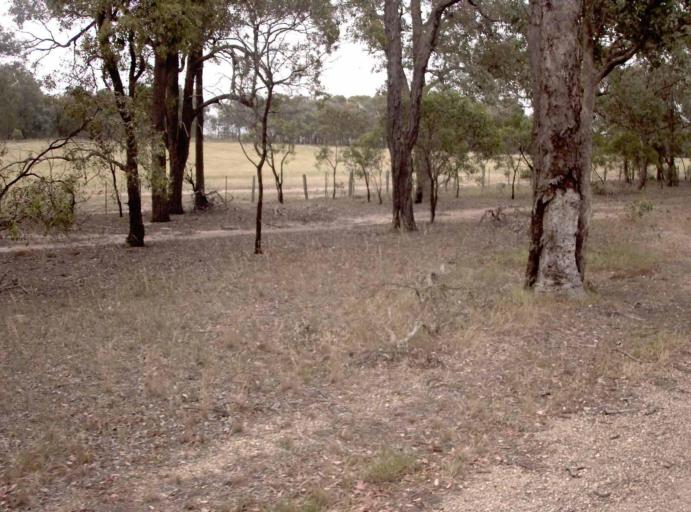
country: AU
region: Victoria
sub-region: Wellington
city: Heyfield
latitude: -37.9597
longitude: 146.7732
